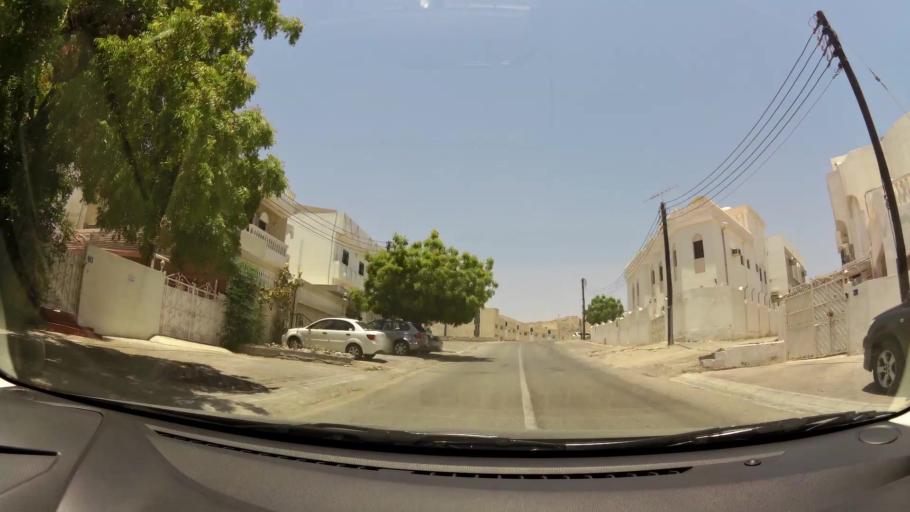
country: OM
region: Muhafazat Masqat
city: Muscat
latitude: 23.6132
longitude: 58.5414
